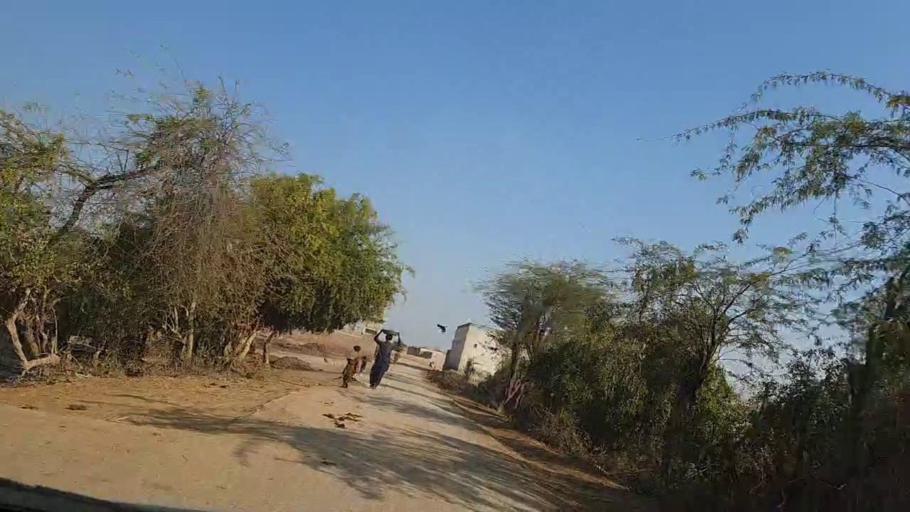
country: PK
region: Sindh
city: Sakrand
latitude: 26.0202
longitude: 68.3318
